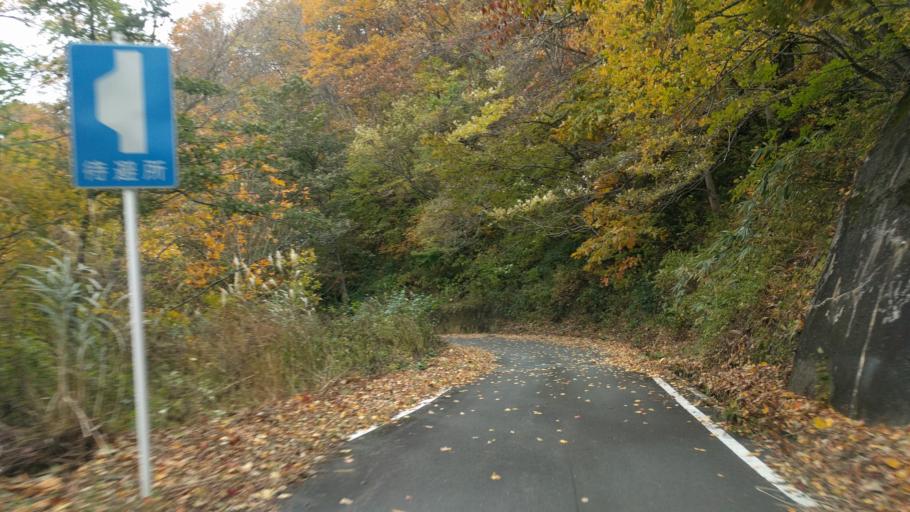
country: JP
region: Fukushima
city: Kitakata
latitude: 37.3854
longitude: 139.7272
